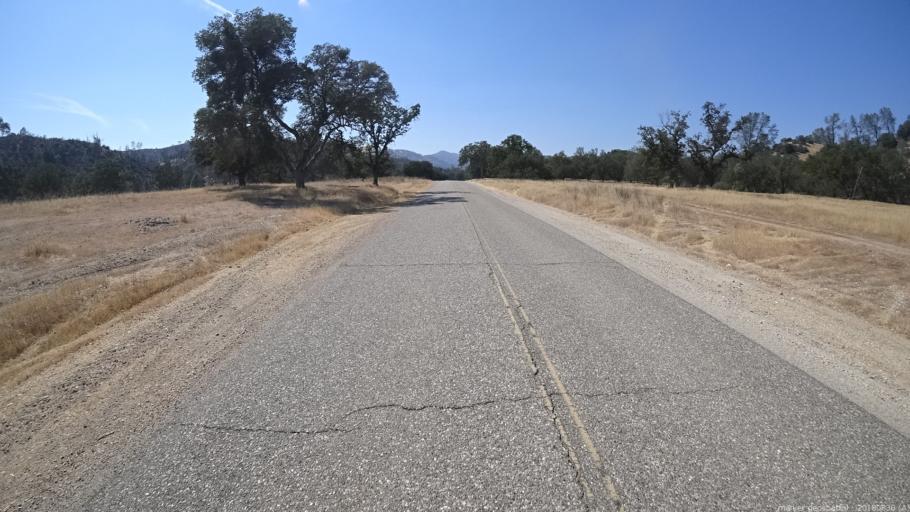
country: US
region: California
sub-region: Monterey County
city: King City
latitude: 36.0009
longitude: -121.2577
